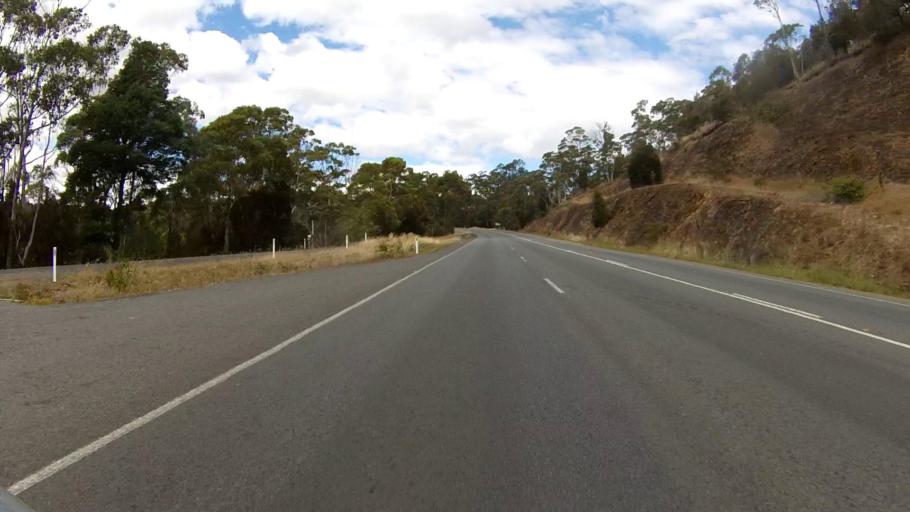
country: AU
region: Tasmania
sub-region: Huon Valley
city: Huonville
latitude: -42.9787
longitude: 147.1106
